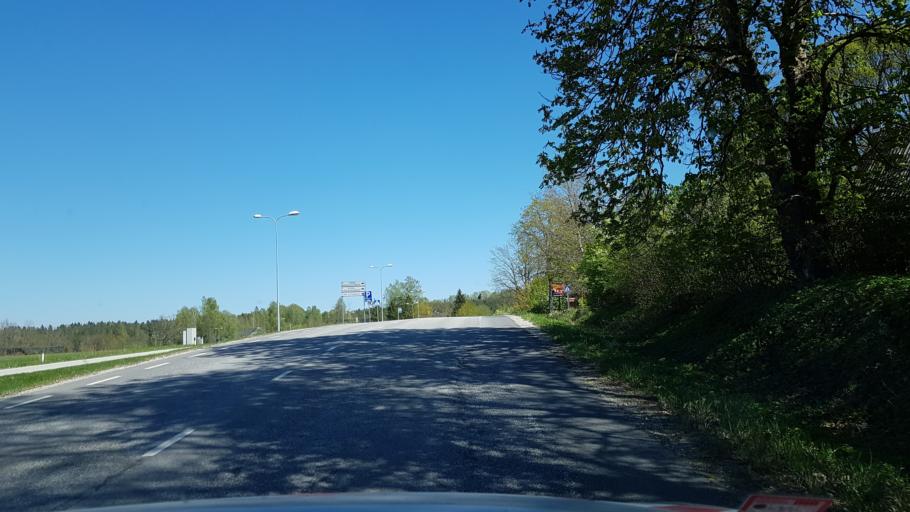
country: EE
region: Tartu
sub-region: Elva linn
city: Elva
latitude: 58.0473
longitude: 26.4723
